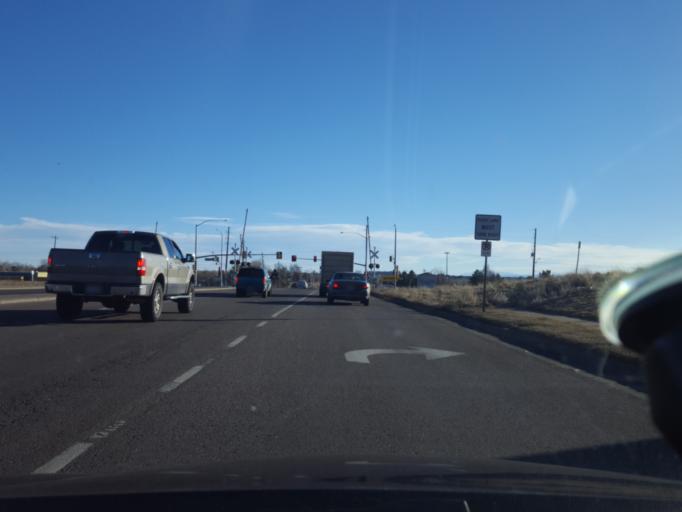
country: US
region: Colorado
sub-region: Adams County
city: Aurora
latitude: 39.7550
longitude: -104.7725
